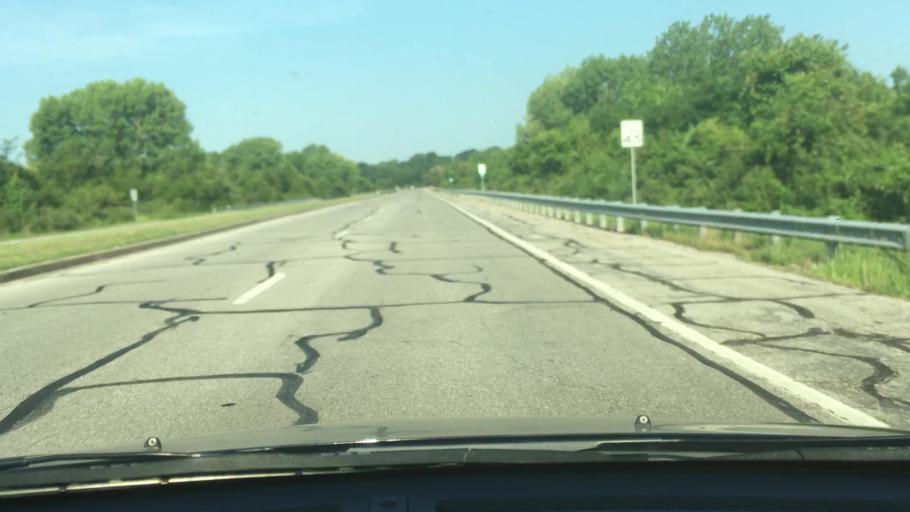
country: US
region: Missouri
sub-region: Jackson County
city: Lees Summit
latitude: 38.8912
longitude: -94.4515
